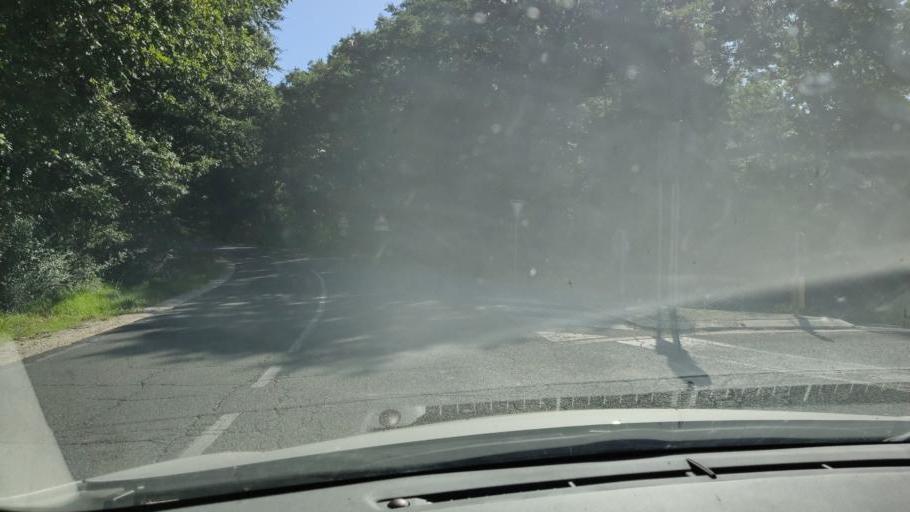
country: IT
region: Umbria
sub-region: Provincia di Terni
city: Avigliano Umbro
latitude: 42.6406
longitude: 12.4171
